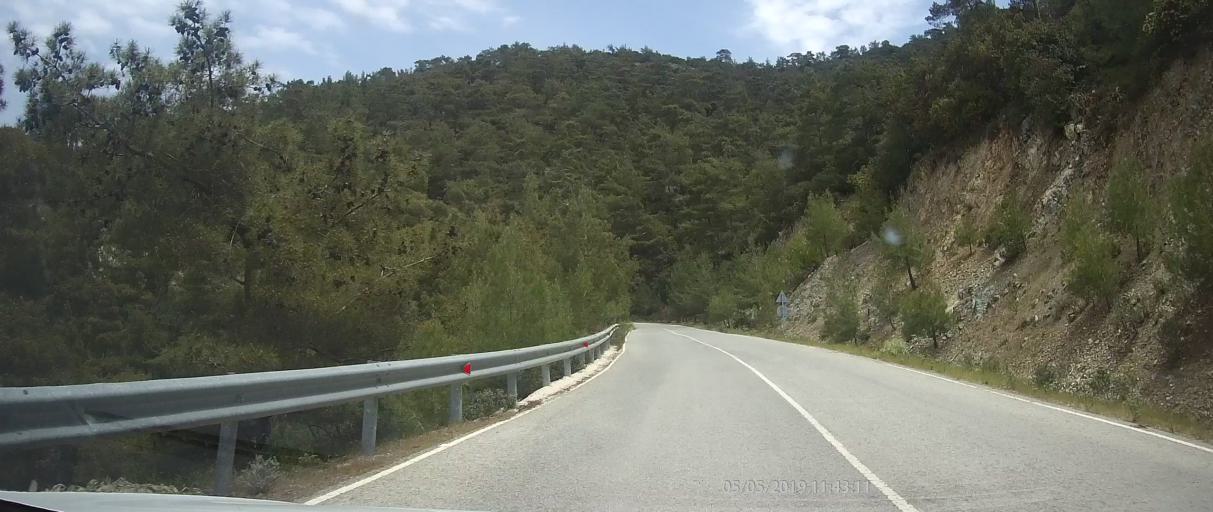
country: CY
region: Lefkosia
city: Kato Pyrgos
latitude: 35.0066
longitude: 32.6702
